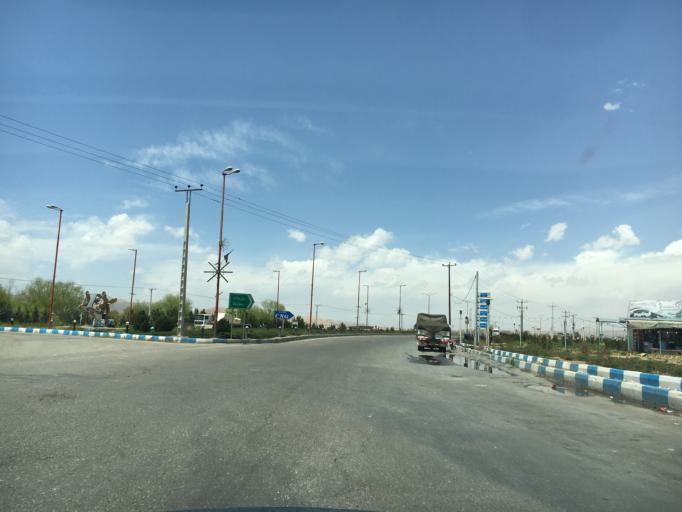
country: IR
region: Isfahan
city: Kashan
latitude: 33.4527
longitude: 51.1722
